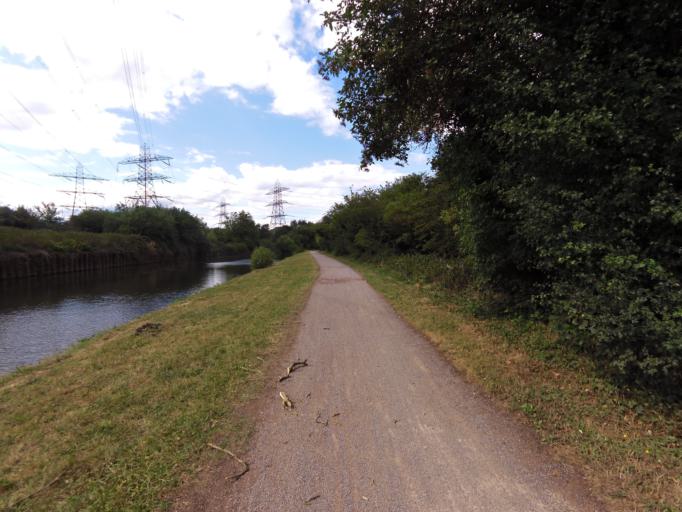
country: GB
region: England
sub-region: Essex
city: Waltham Abbey
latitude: 51.6622
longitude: -0.0204
